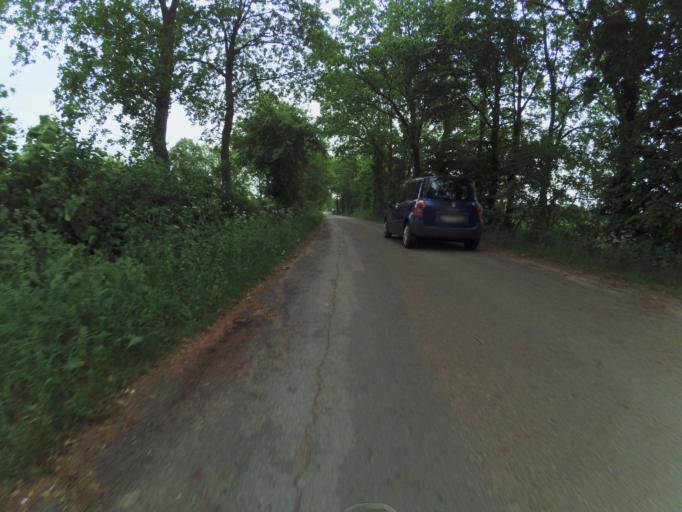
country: DE
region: North Rhine-Westphalia
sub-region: Regierungsbezirk Munster
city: Birgte
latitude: 52.2893
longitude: 7.6561
